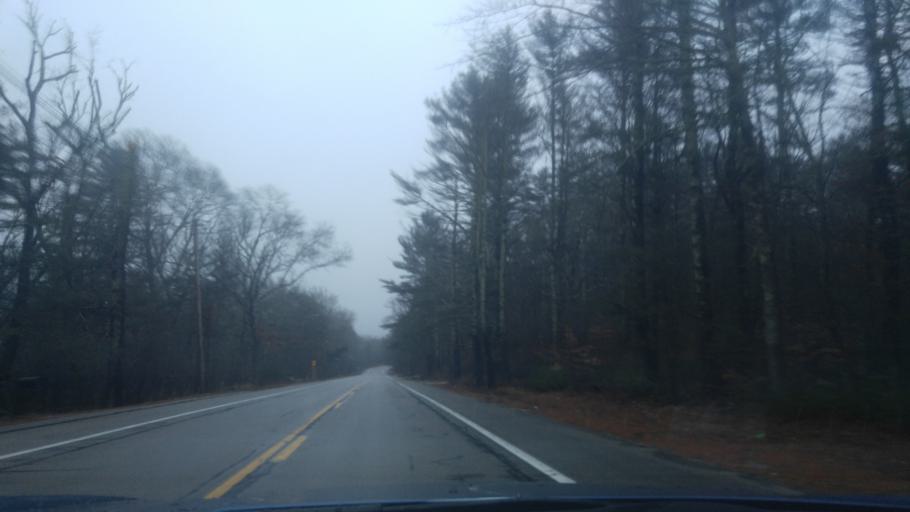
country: US
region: Rhode Island
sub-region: Washington County
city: Charlestown
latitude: 41.4639
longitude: -71.6196
